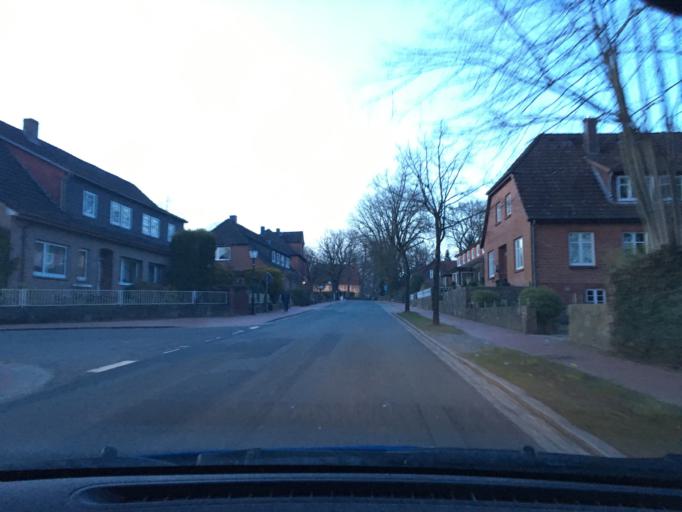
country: DE
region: Lower Saxony
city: Egestorf
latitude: 53.1914
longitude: 10.0629
